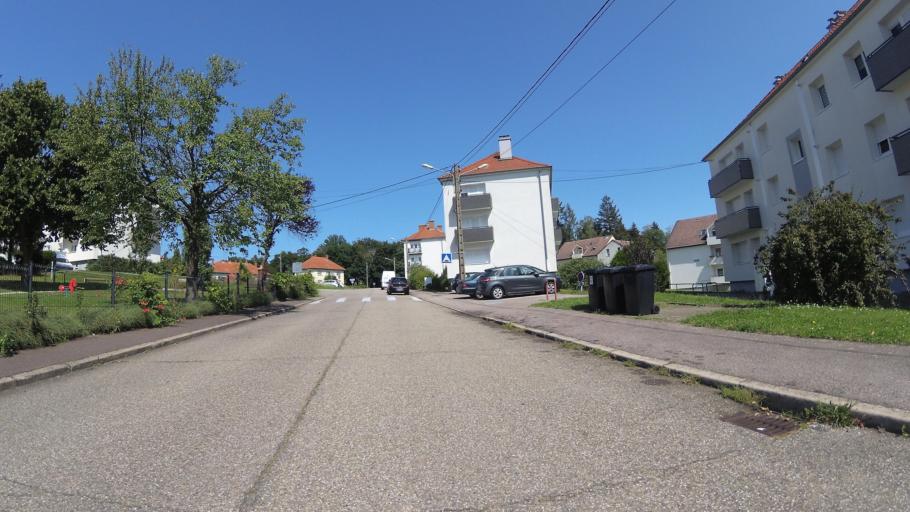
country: FR
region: Lorraine
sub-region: Departement de la Moselle
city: Spicheren
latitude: 49.2048
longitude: 6.9532
